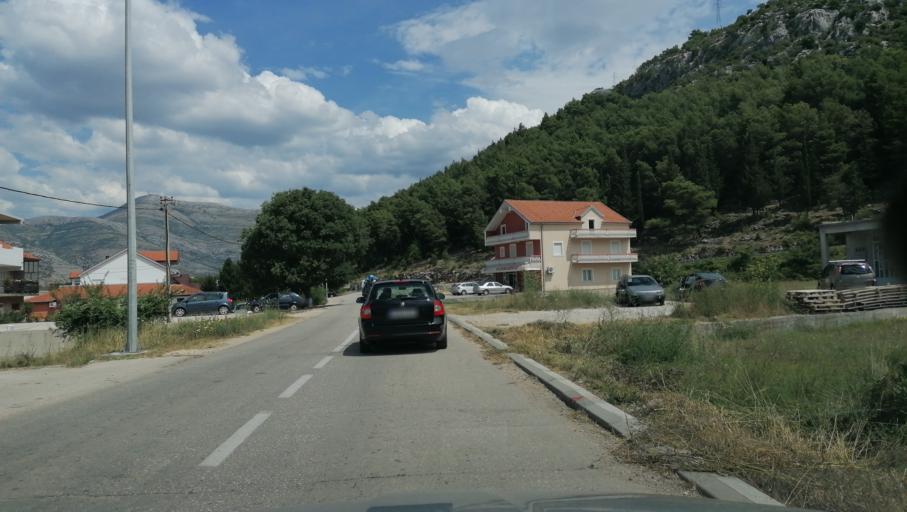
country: BA
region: Republika Srpska
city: Trebinje
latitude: 42.6844
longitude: 18.3356
